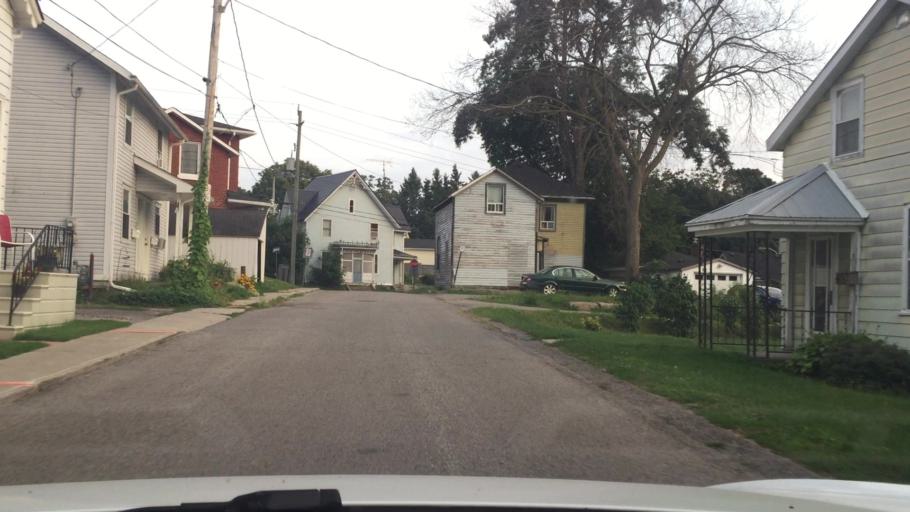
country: CA
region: Ontario
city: Cobourg
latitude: 43.9540
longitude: -78.2920
